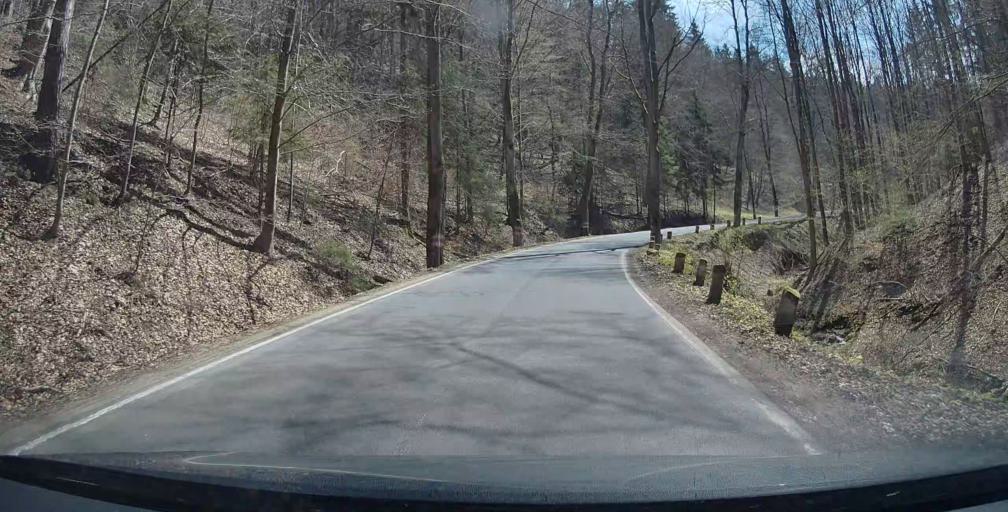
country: PL
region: Lower Silesian Voivodeship
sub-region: Powiat klodzki
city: Kudowa-Zdroj
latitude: 50.4475
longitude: 16.2732
